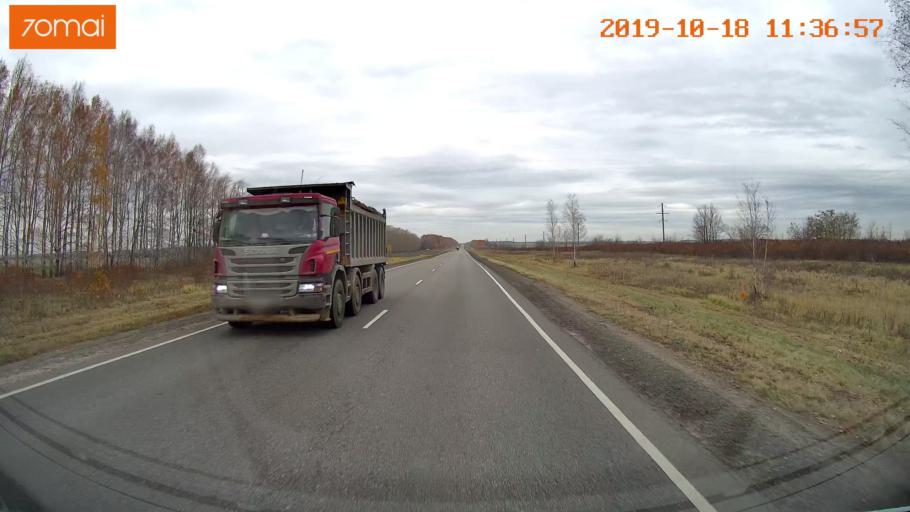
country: RU
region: Rjazan
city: Oktyabr'skiy
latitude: 54.1463
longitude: 38.8187
